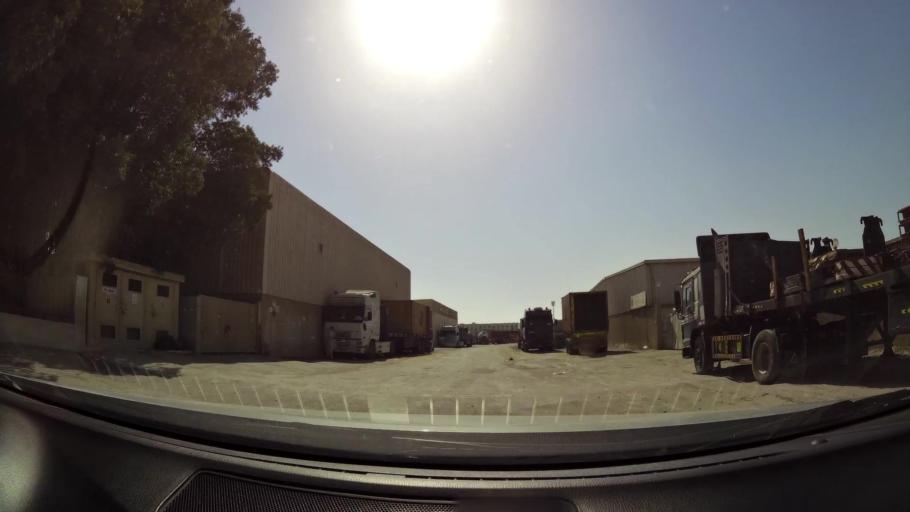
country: AE
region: Dubai
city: Dubai
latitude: 25.0066
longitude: 55.1152
